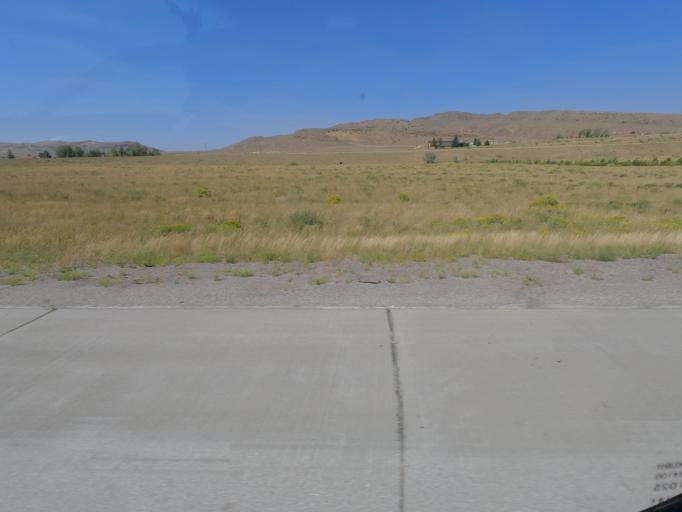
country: US
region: Wyoming
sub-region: Carbon County
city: Rawlins
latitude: 41.7817
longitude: -107.2690
